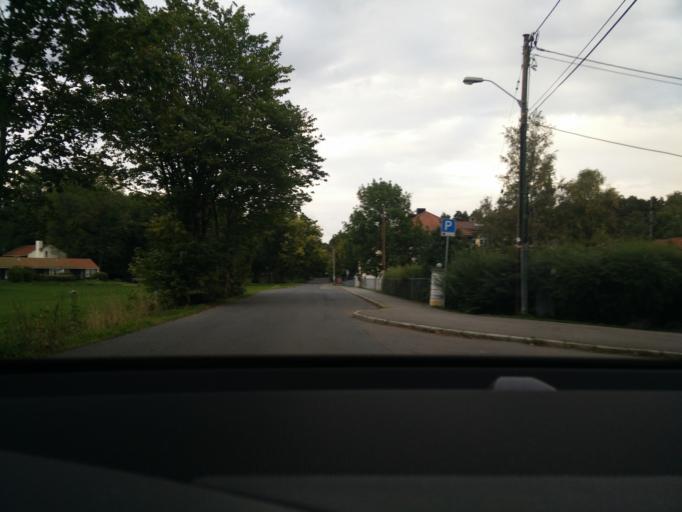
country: NO
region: Oslo
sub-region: Oslo
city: Sjolyststranda
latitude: 59.9043
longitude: 10.6758
